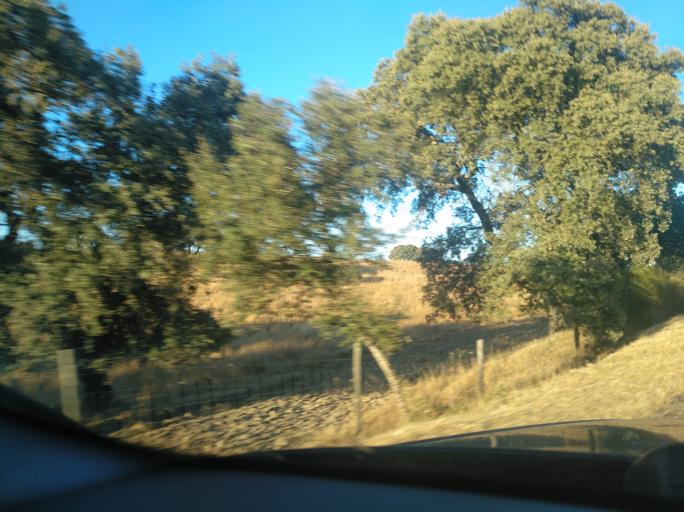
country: PT
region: Portalegre
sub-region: Arronches
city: Arronches
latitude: 39.0698
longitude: -7.2354
